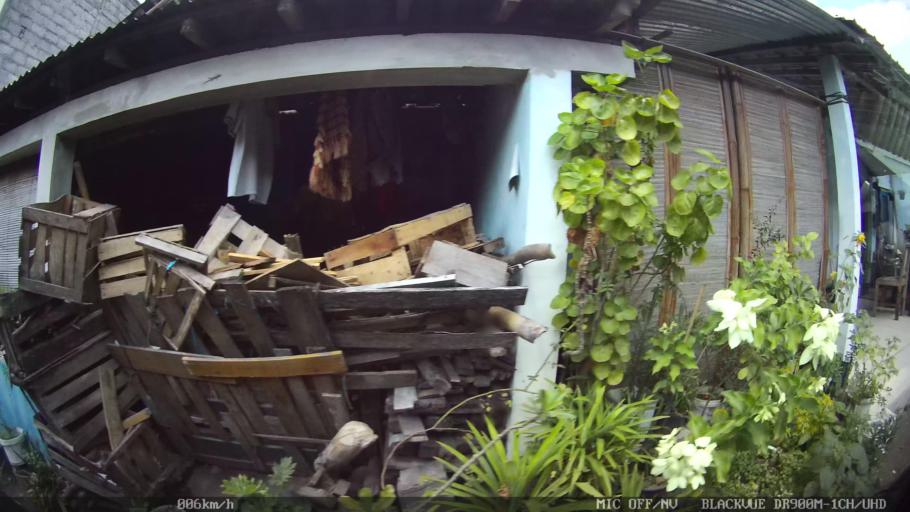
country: ID
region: Daerah Istimewa Yogyakarta
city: Kasihan
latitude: -7.8152
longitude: 110.3474
